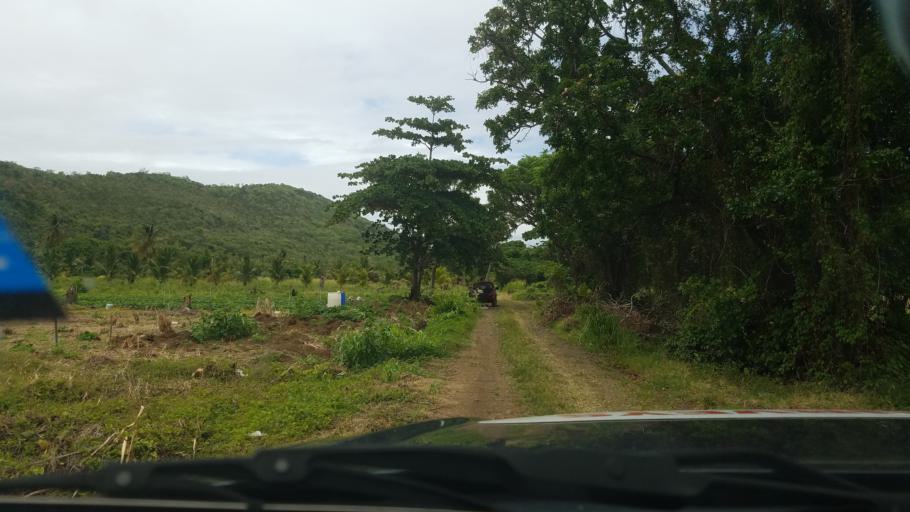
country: LC
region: Gros-Islet
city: Gros Islet
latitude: 14.0287
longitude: -60.9053
